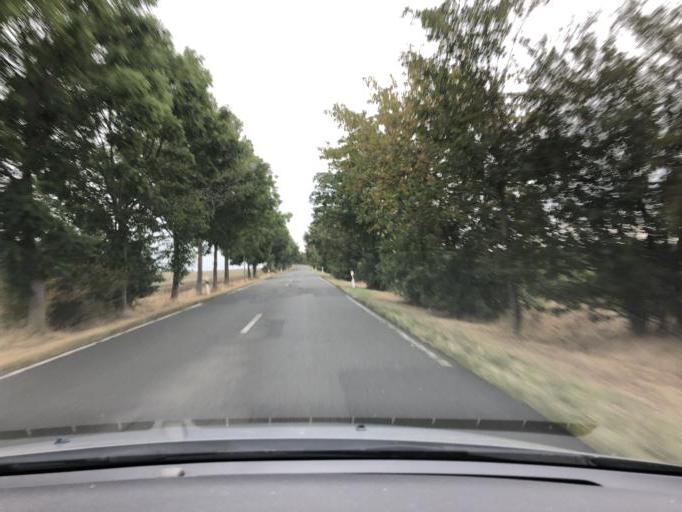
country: DE
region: Saxony-Anhalt
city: Brumby
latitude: 51.8649
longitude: 11.7116
